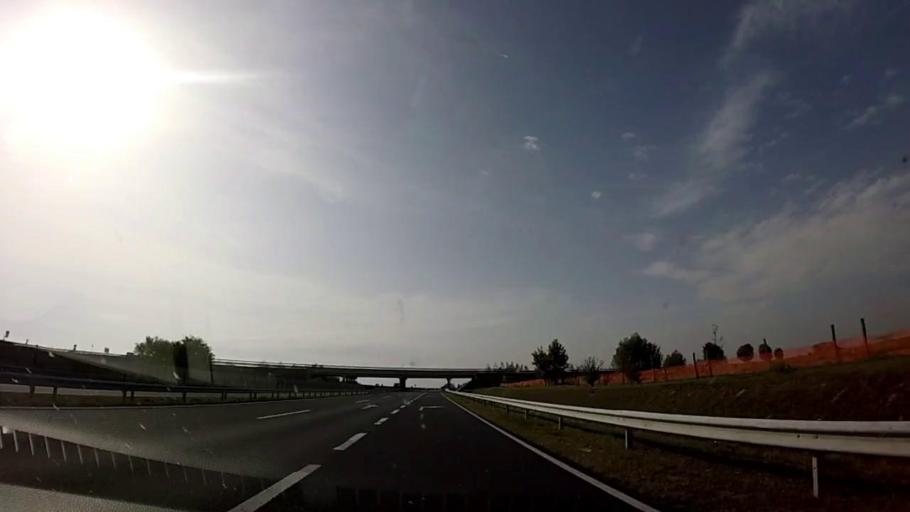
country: HU
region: Zala
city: Murakeresztur
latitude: 46.4594
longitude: 16.8884
